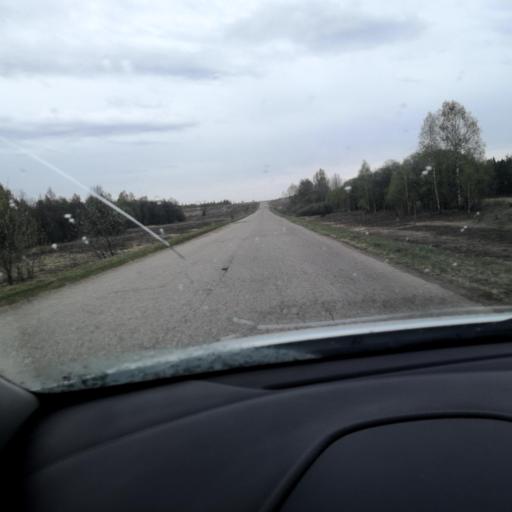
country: RU
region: Bashkortostan
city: Pavlovka
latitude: 55.3897
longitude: 56.4452
